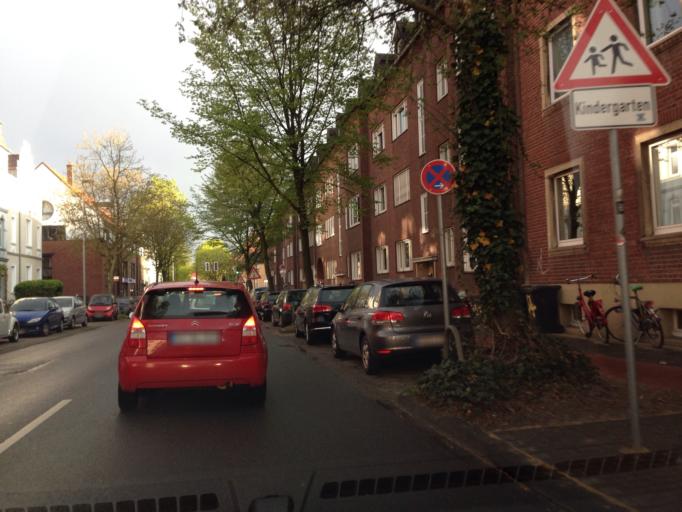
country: DE
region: North Rhine-Westphalia
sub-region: Regierungsbezirk Munster
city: Muenster
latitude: 51.9489
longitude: 7.6218
